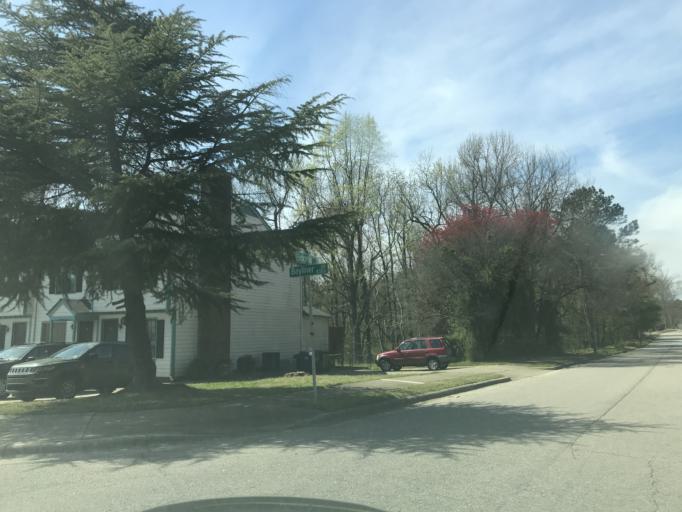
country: US
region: North Carolina
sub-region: Wake County
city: Raleigh
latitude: 35.8415
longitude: -78.5958
